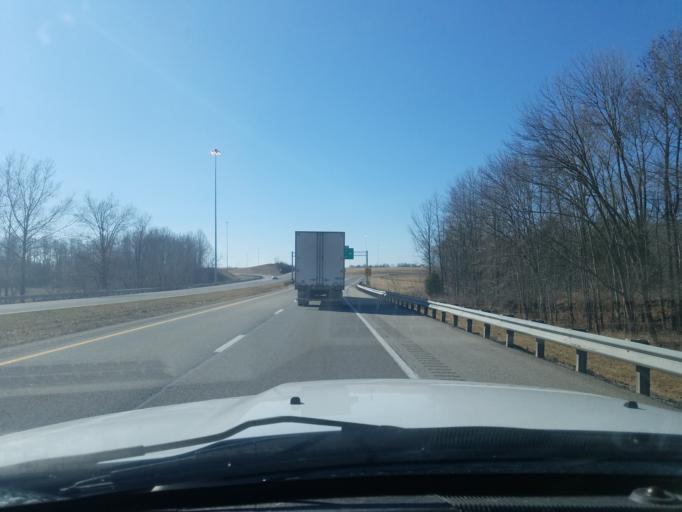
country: US
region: Kentucky
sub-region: Ohio County
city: Oak Grove
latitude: 37.3880
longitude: -86.8029
